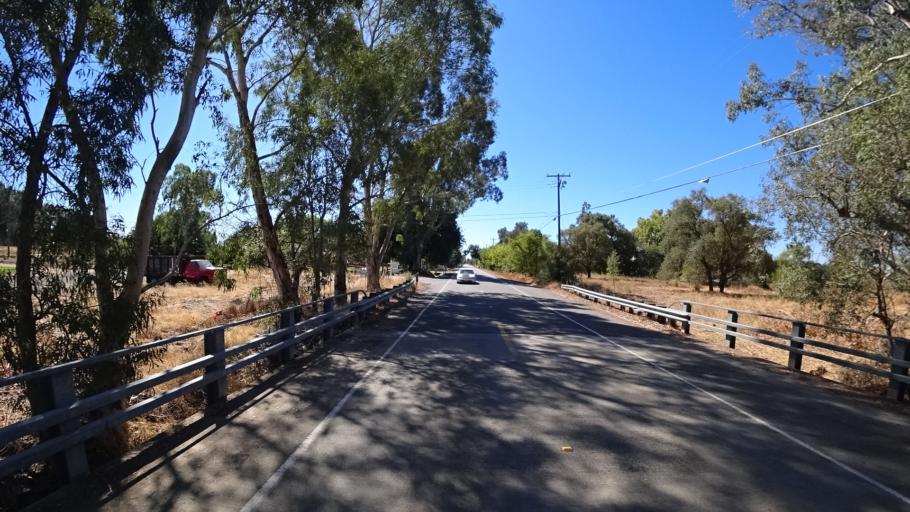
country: US
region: California
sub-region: Sacramento County
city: Vineyard
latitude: 38.4440
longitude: -121.3253
